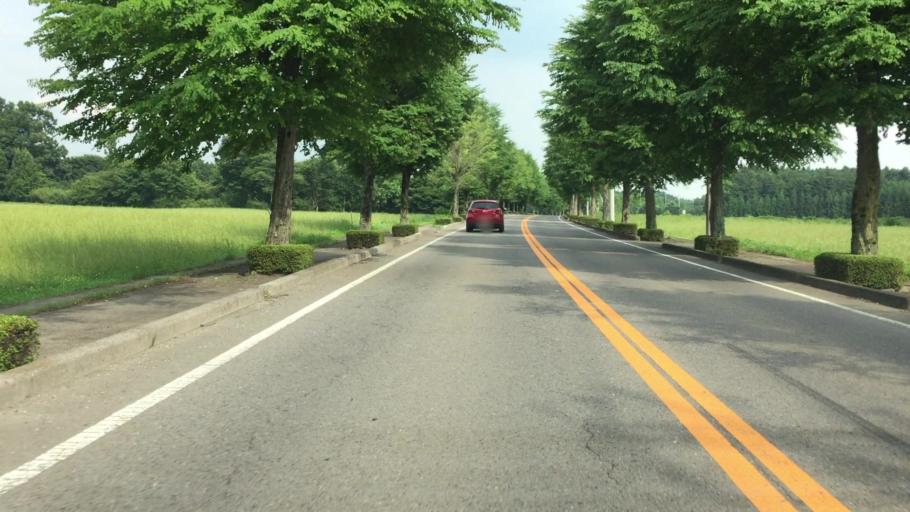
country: JP
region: Tochigi
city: Kuroiso
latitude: 36.9873
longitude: 139.9540
